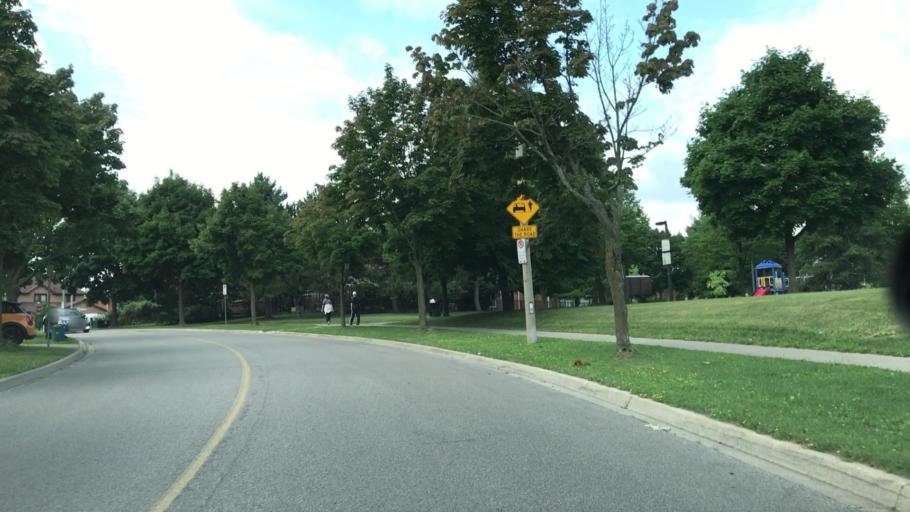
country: CA
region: Ontario
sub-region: York
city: Richmond Hill
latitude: 43.8455
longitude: -79.3996
